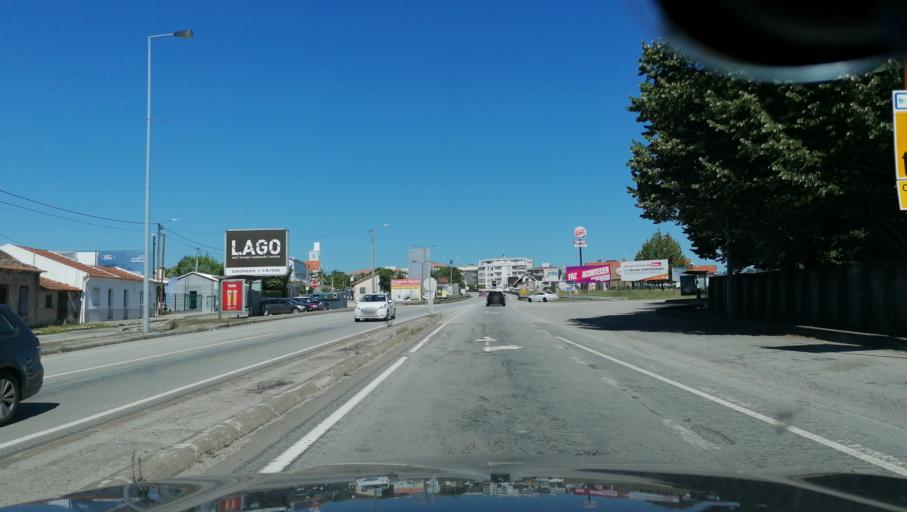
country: PT
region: Aveiro
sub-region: Santa Maria da Feira
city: Feira
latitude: 40.9257
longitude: -8.5620
